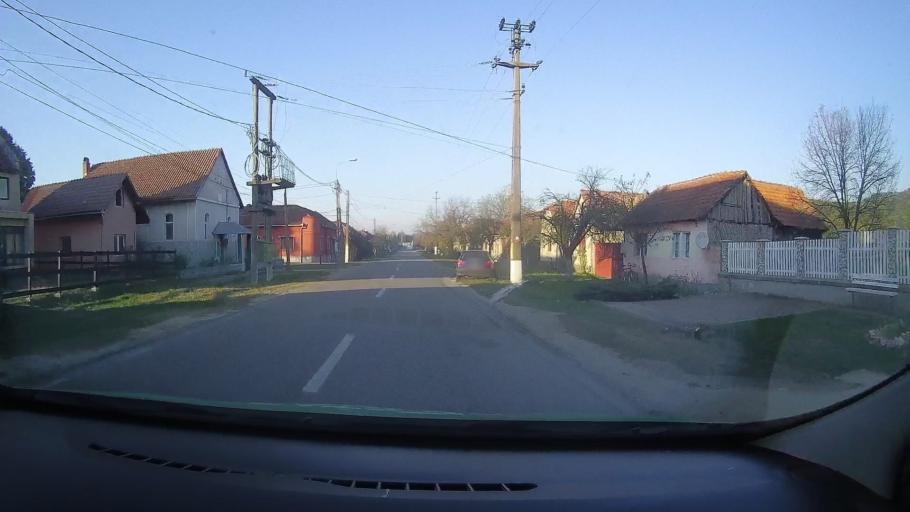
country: RO
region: Timis
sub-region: Comuna Fardea
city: Fardea
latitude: 45.7386
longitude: 22.1640
